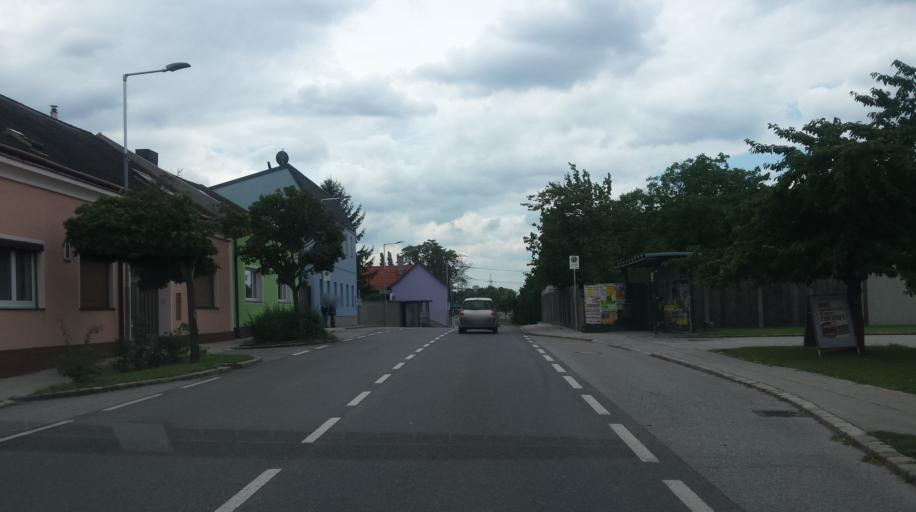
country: AT
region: Lower Austria
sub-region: Politischer Bezirk Wien-Umgebung
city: Zwolfaxing
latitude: 48.0985
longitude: 16.4551
